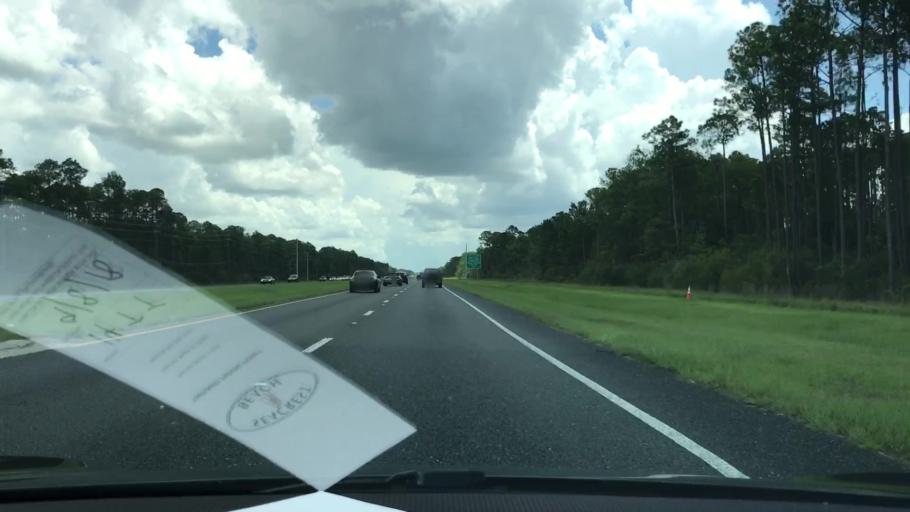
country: US
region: Florida
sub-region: Walton County
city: Seaside
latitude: 30.3677
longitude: -86.1914
